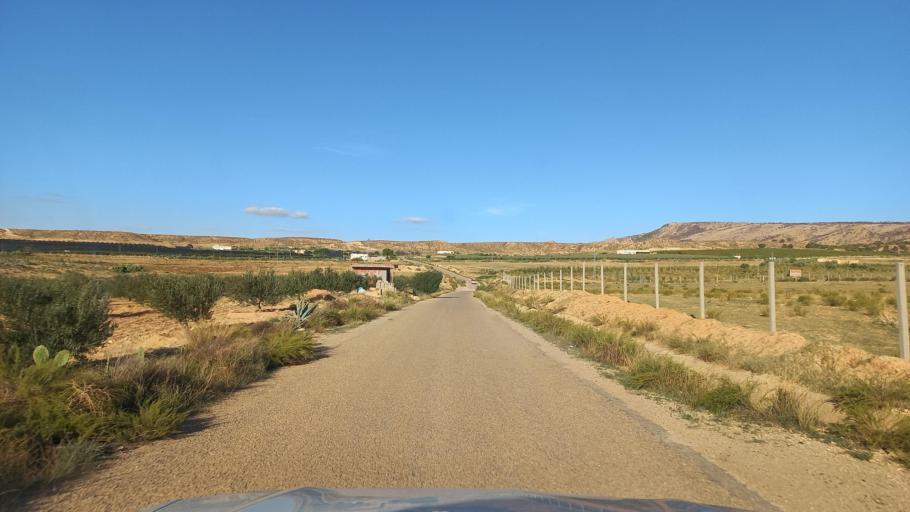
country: TN
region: Al Qasrayn
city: Sbiba
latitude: 35.3423
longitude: 9.1231
